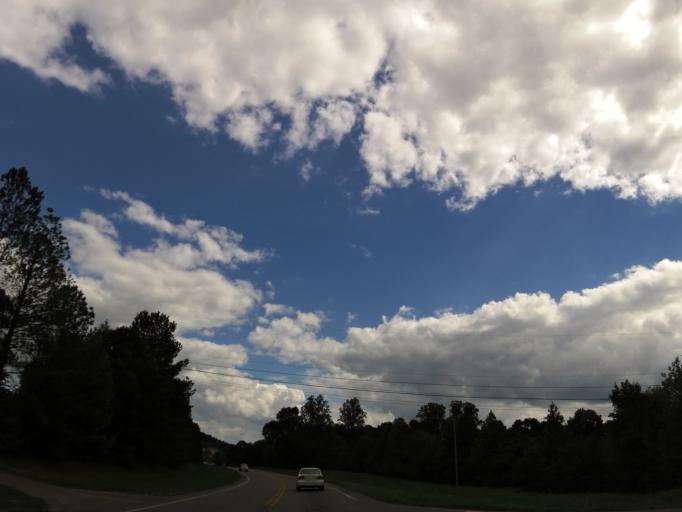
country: US
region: Georgia
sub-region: Walker County
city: Lookout Mountain
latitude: 34.9646
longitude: -85.3386
